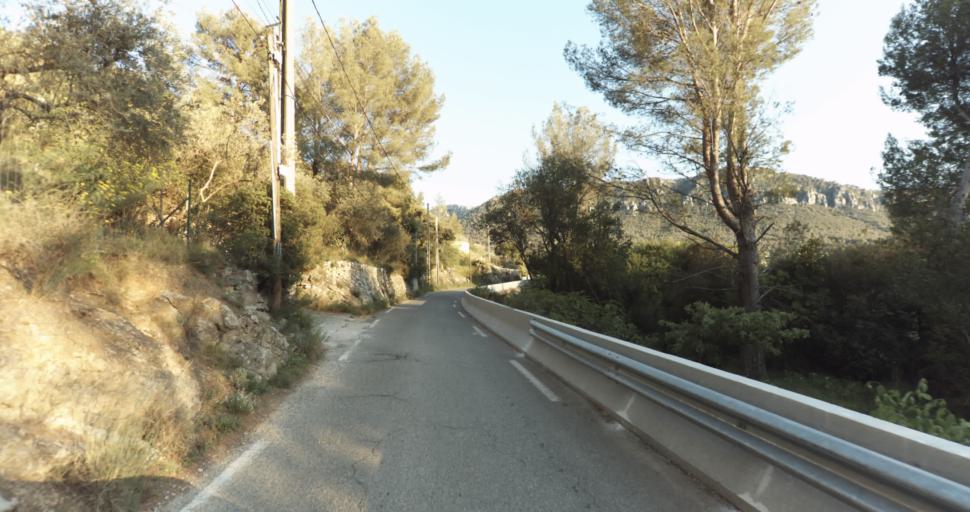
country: FR
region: Provence-Alpes-Cote d'Azur
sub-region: Departement du Var
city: Le Revest-les-Eaux
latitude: 43.1700
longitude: 5.9343
